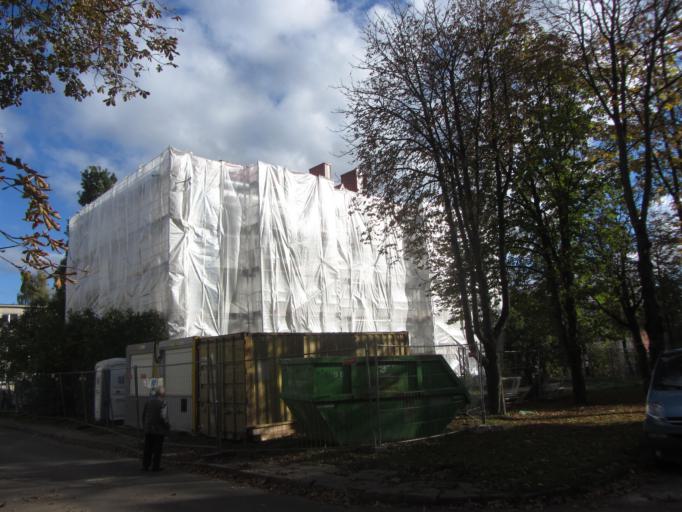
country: LT
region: Vilnius County
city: Lazdynai
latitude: 54.6695
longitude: 25.2160
